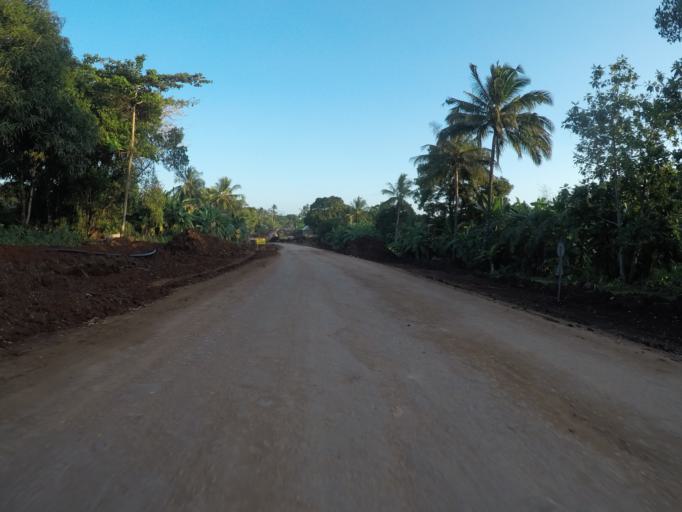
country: TZ
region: Zanzibar North
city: Gamba
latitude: -5.9170
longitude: 39.2992
